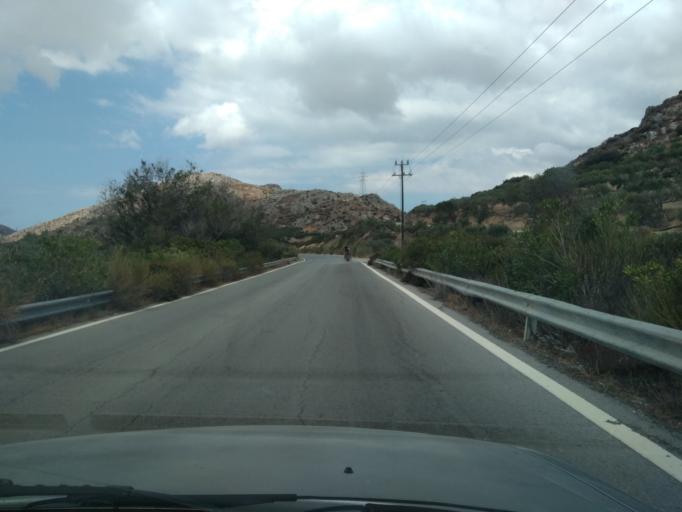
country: GR
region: Crete
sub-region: Nomos Lasithiou
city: Makry-Gialos
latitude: 35.0596
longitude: 26.0385
